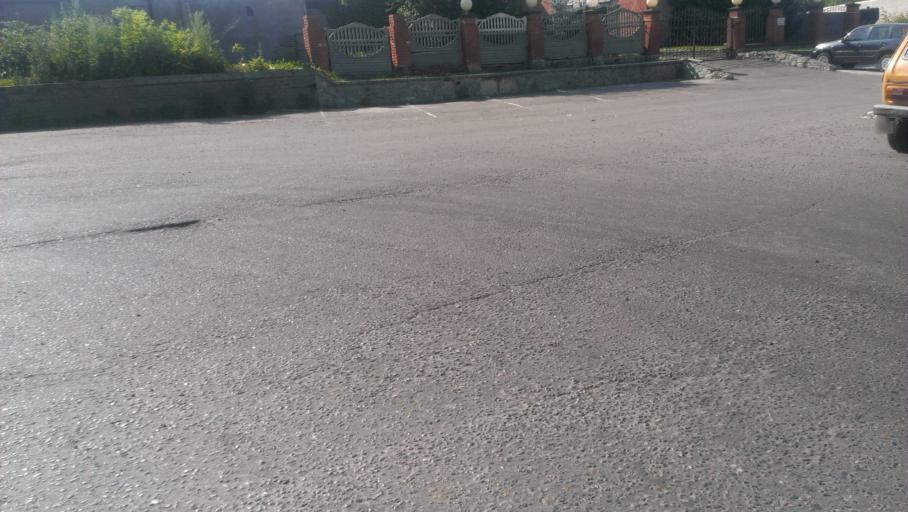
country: RU
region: Altai Krai
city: Novosilikatnyy
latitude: 53.3836
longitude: 83.6710
